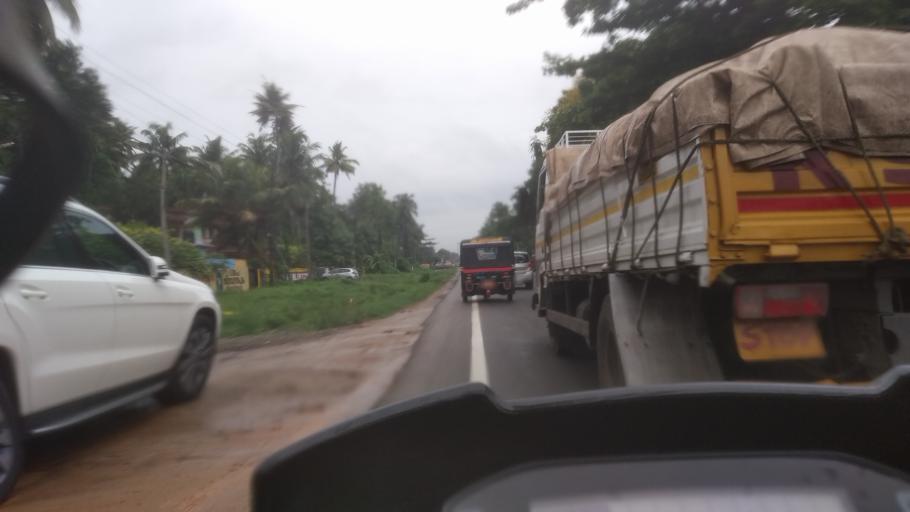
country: IN
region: Kerala
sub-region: Alappuzha
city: Kayankulam
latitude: 9.1670
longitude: 76.5009
